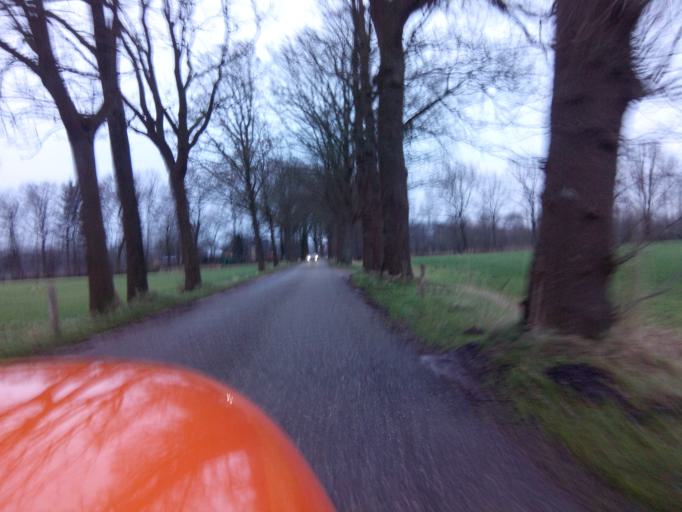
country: NL
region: Utrecht
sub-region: Gemeente Leusden
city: Leusden
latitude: 52.1496
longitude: 5.4600
